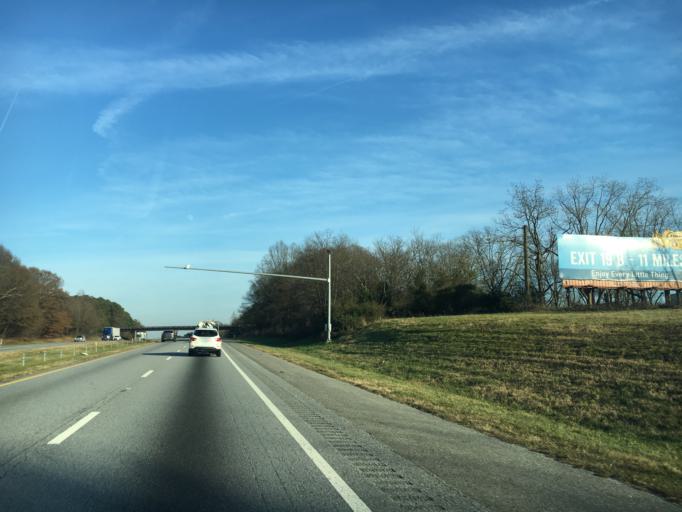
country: US
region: Georgia
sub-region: Hart County
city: Reed Creek
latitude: 34.5150
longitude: -82.8848
